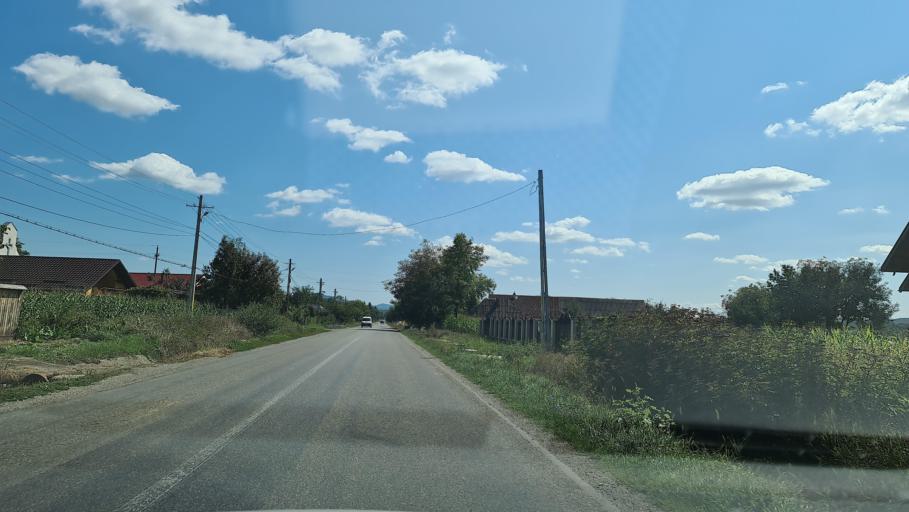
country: RO
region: Bacau
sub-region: Comuna Sanduleni
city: Versesti
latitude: 46.4801
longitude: 26.7024
